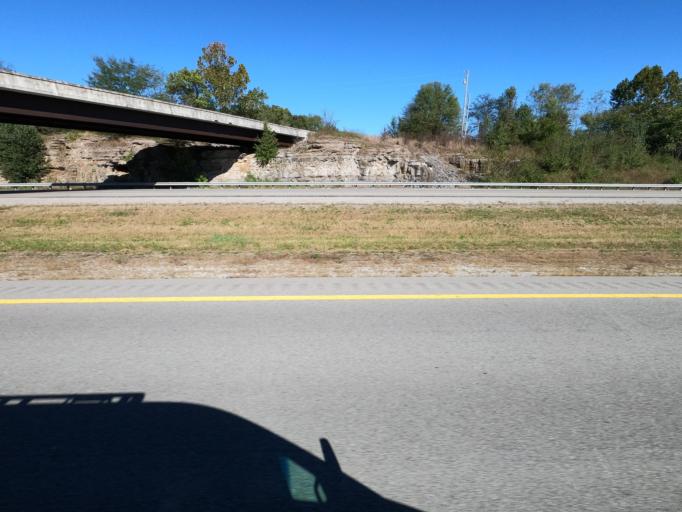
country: US
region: Tennessee
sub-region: Williamson County
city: Thompson's Station
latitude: 35.8227
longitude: -86.9122
